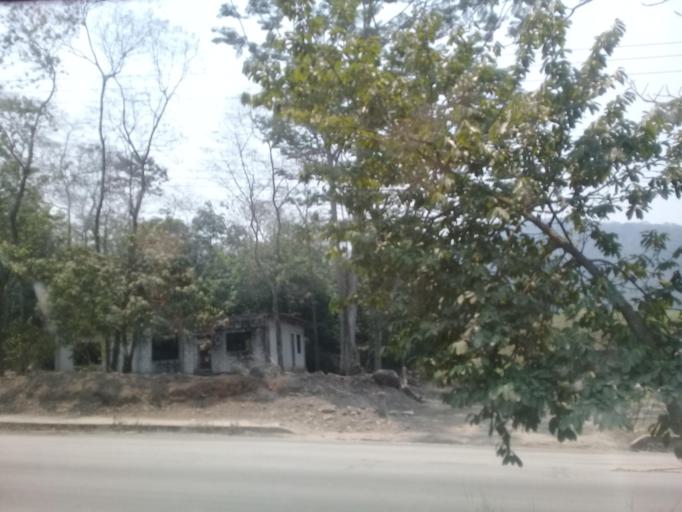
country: MX
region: Veracruz
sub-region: Tezonapa
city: Laguna Chica (Pueblo Nuevo)
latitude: 18.5515
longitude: -96.7276
